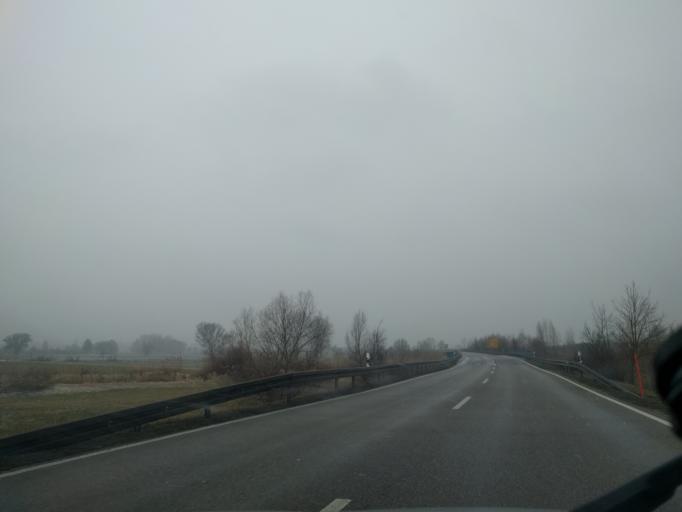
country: DE
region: Bavaria
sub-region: Swabia
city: Asbach-Baumenheim
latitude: 48.6965
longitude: 10.7954
